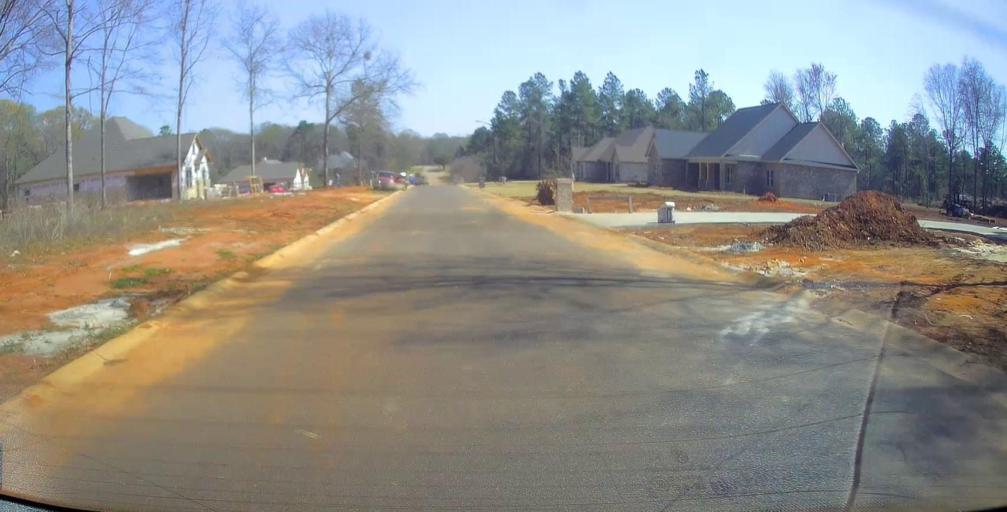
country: US
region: Georgia
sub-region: Peach County
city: Byron
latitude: 32.5976
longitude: -83.7556
